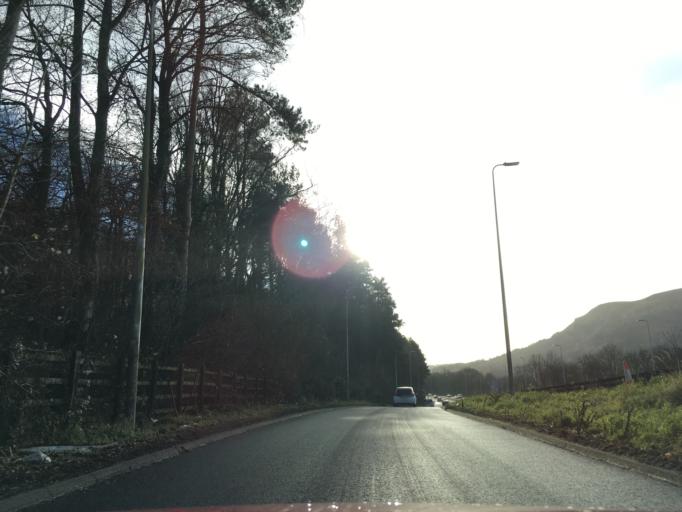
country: GB
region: Wales
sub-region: Caerphilly County Borough
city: Abertridwr
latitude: 51.5588
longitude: -3.2687
